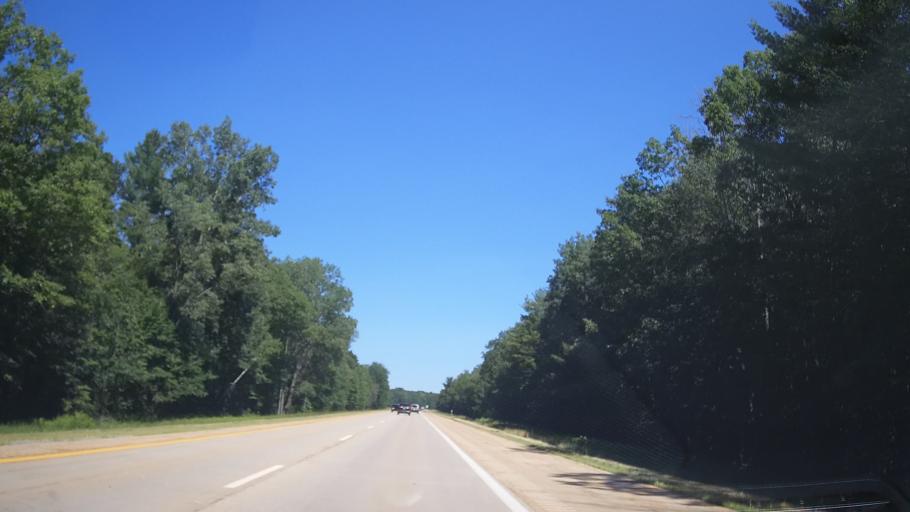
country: US
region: Michigan
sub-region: Midland County
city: Coleman
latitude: 43.7027
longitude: -84.4357
